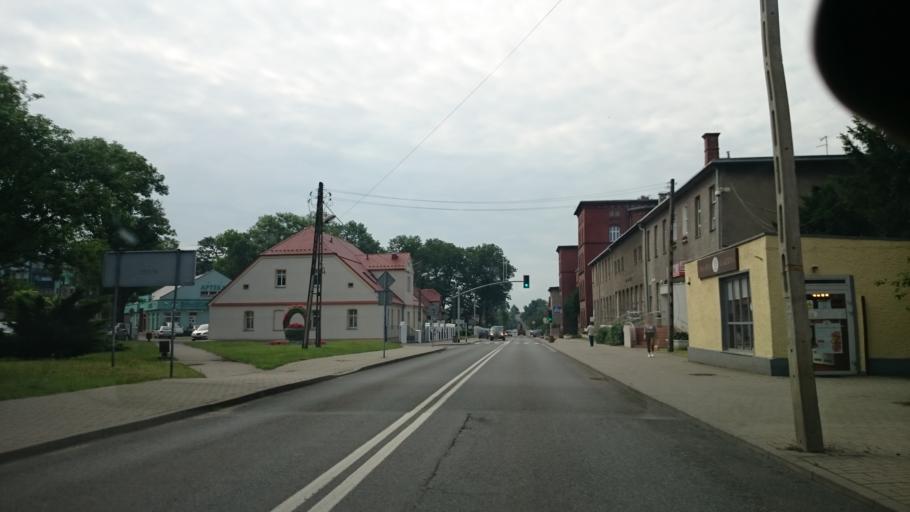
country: PL
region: Silesian Voivodeship
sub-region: Powiat gliwicki
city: Toszek
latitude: 50.4541
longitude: 18.5223
